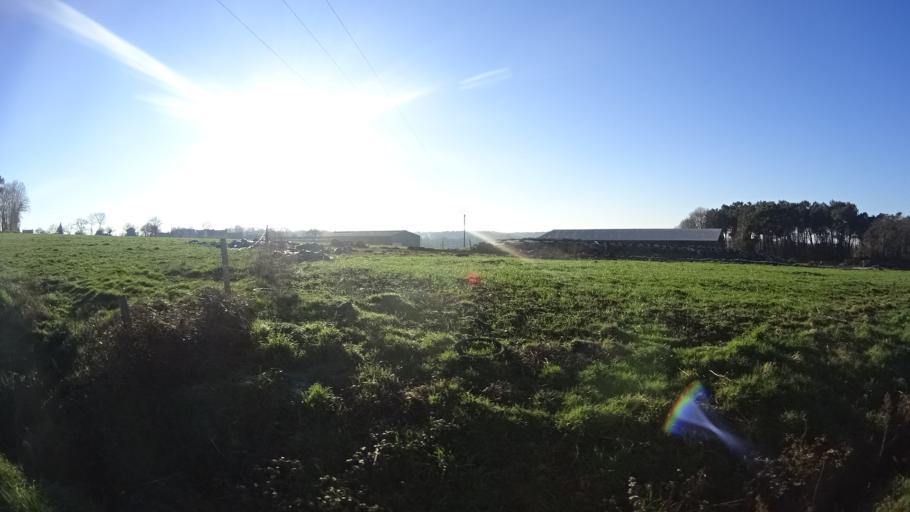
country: FR
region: Brittany
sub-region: Departement du Morbihan
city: Allaire
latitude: 47.6596
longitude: -2.1751
